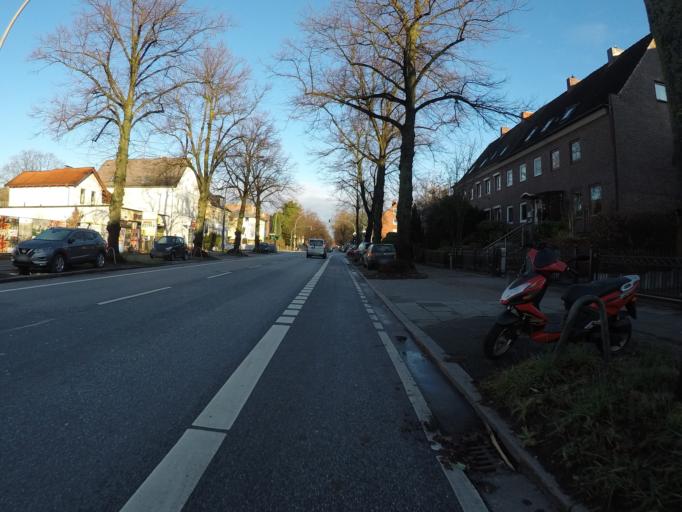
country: DE
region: Hamburg
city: Fuhlsbuettel
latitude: 53.6284
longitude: 10.0135
